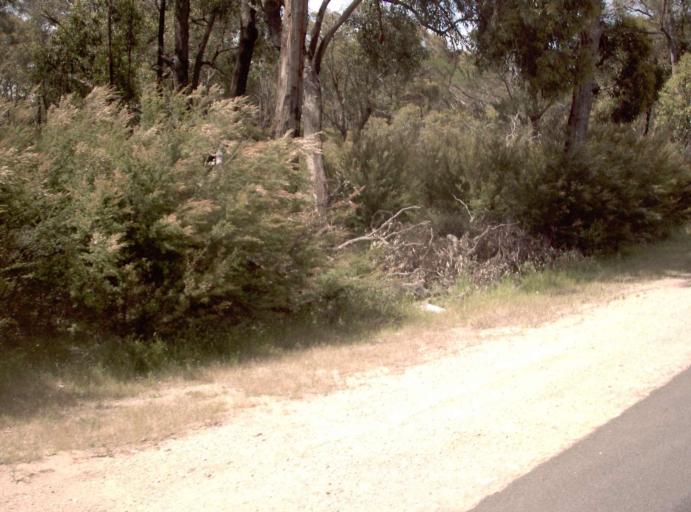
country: AU
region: Victoria
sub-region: Wellington
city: Sale
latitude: -37.9209
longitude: 147.2806
